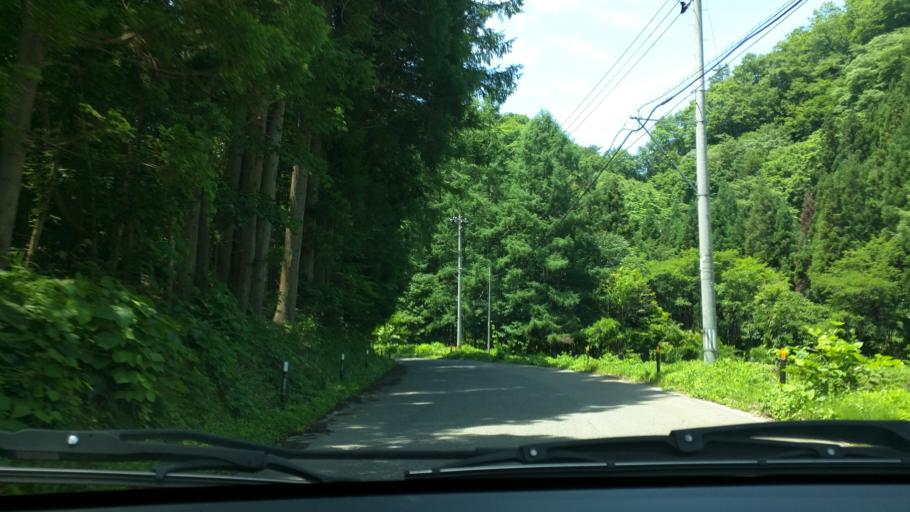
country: JP
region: Tochigi
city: Kuroiso
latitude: 37.2571
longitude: 139.7840
